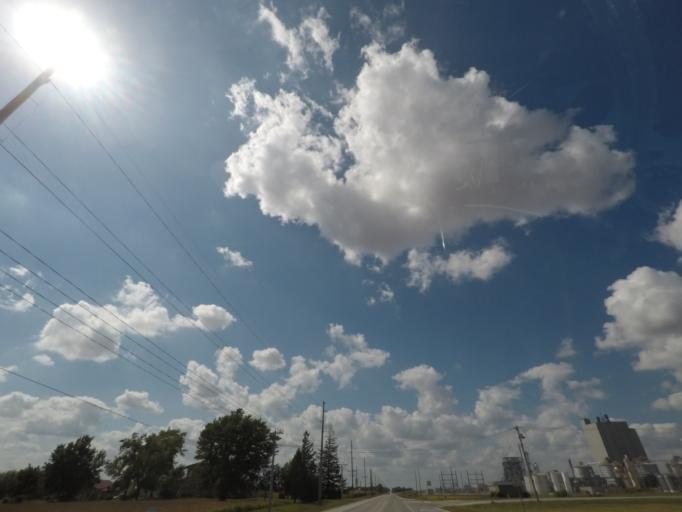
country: US
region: Iowa
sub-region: Story County
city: Nevada
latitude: 42.0231
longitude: -93.5106
